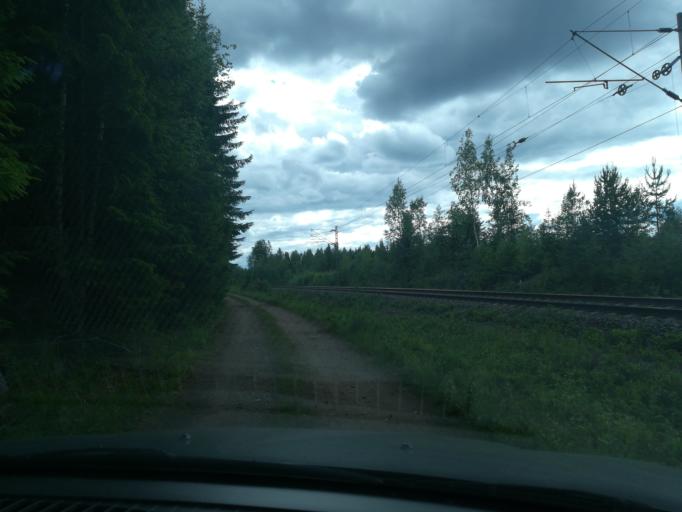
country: FI
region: Southern Savonia
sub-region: Mikkeli
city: Mikkeli
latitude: 61.6745
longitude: 27.1131
